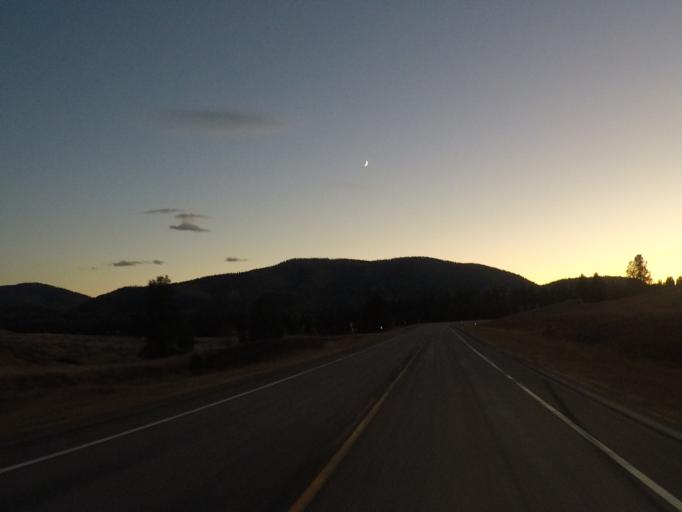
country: US
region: Montana
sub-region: Missoula County
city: Seeley Lake
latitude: 47.0316
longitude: -113.2363
